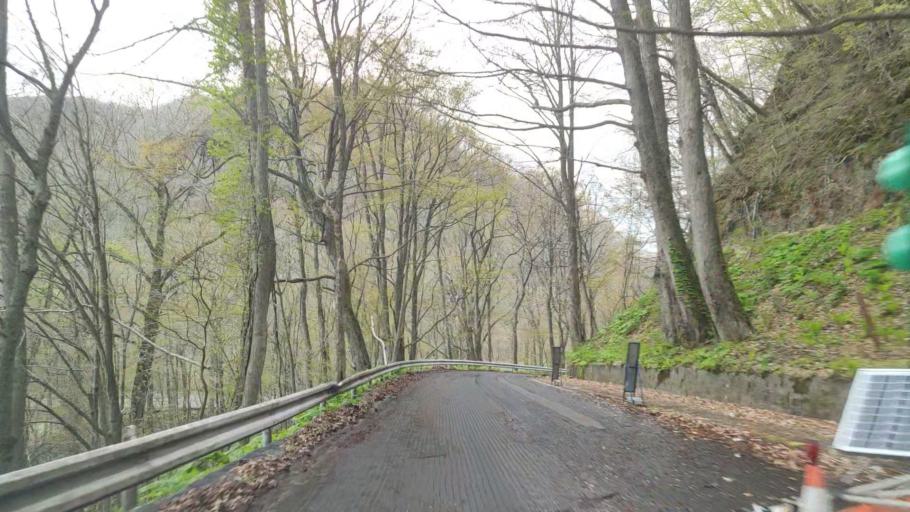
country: JP
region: Akita
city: Hanawa
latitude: 40.4250
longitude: 140.9098
